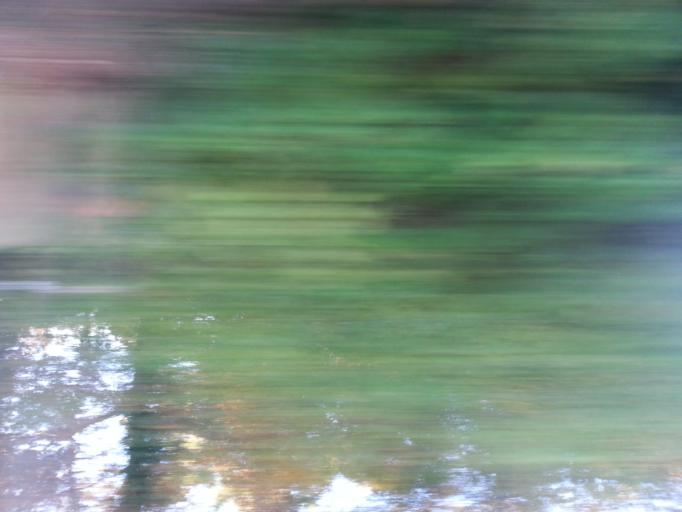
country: US
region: Tennessee
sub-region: Blount County
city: Louisville
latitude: 35.9167
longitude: -84.0186
